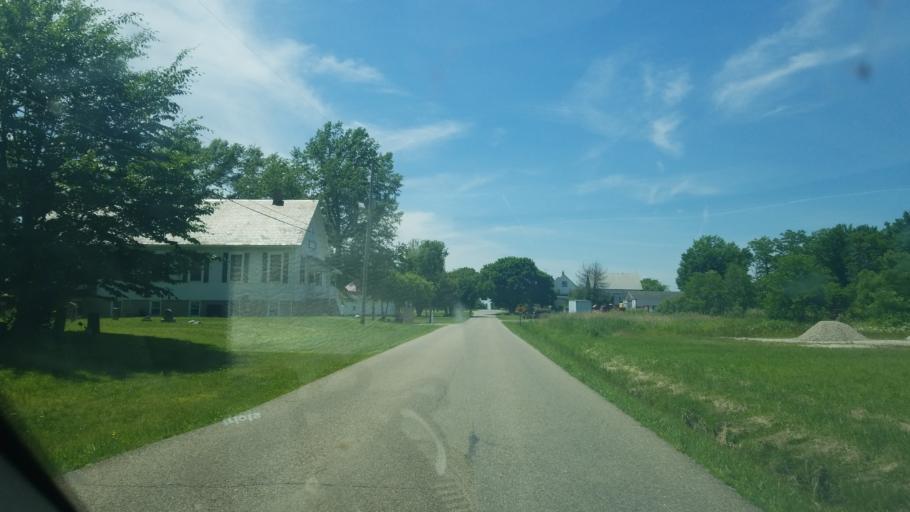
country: US
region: Ohio
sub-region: Stark County
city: Alliance
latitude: 40.8575
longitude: -81.1028
